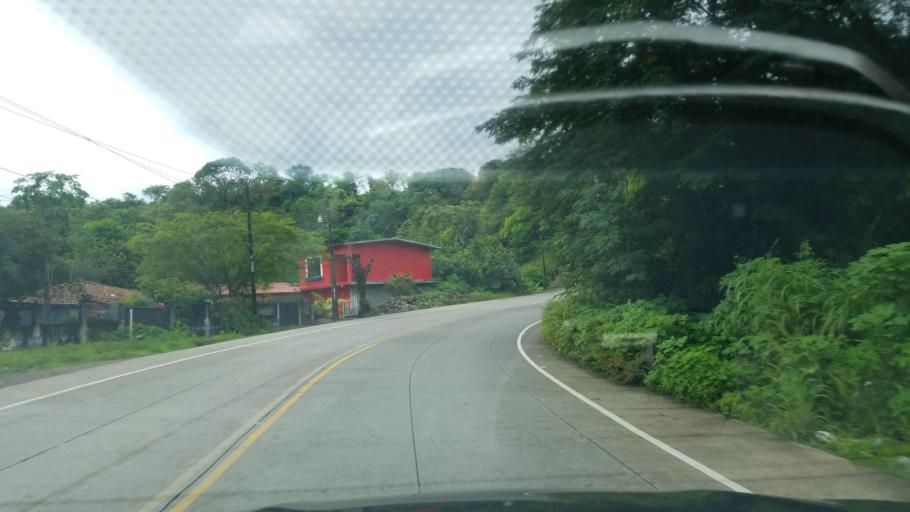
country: HN
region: Choluteca
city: Pespire
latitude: 13.6514
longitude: -87.3653
